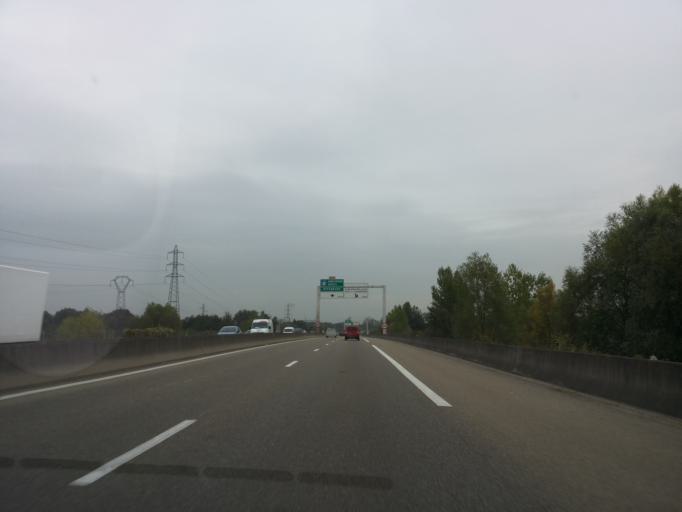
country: FR
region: Alsace
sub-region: Departement du Bas-Rhin
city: Eschau
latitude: 48.4972
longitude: 7.7458
